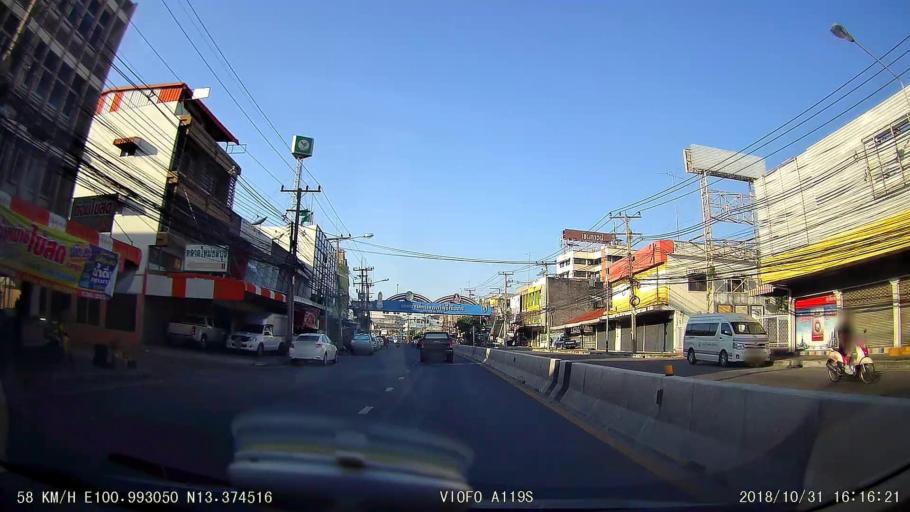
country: TH
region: Chon Buri
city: Chon Buri
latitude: 13.3747
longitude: 100.9931
